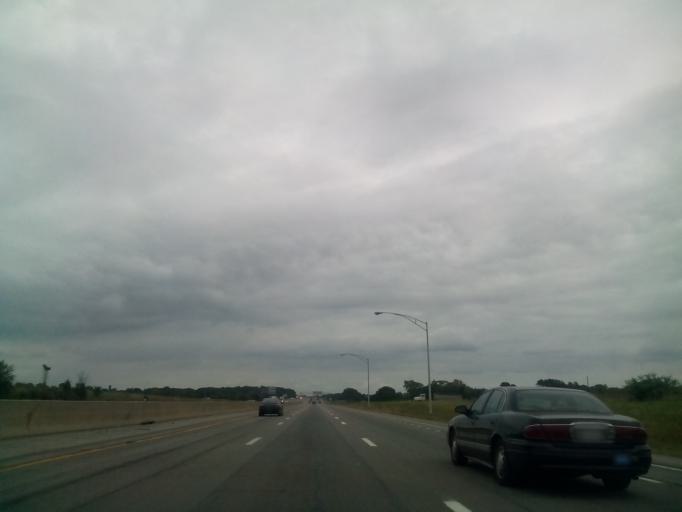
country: US
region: Ohio
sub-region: Huron County
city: Bellevue
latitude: 41.3399
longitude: -82.7576
